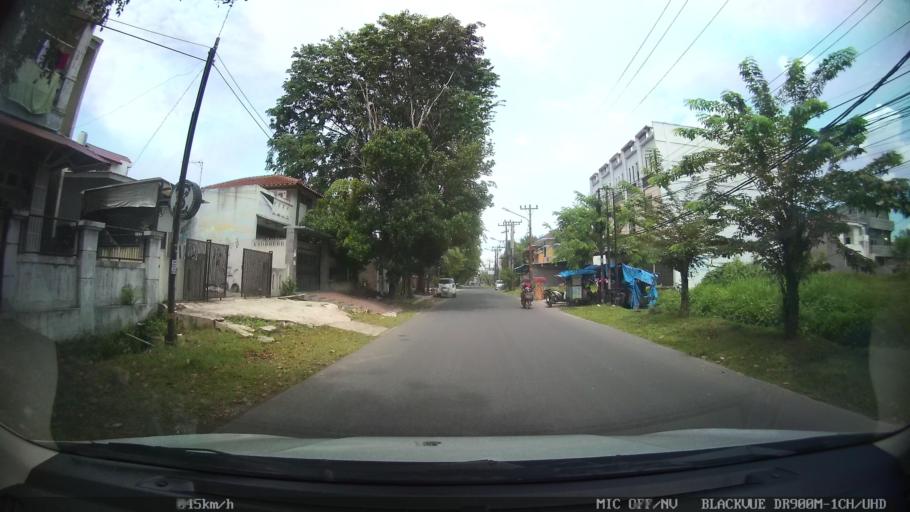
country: ID
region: North Sumatra
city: Sunggal
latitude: 3.5550
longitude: 98.6376
